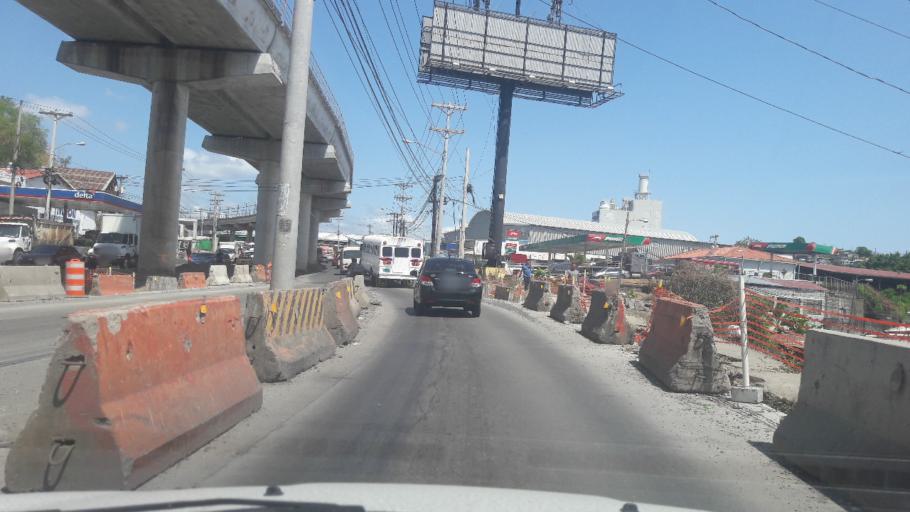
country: PA
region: Panama
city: San Miguelito
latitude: 9.0325
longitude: -79.5054
